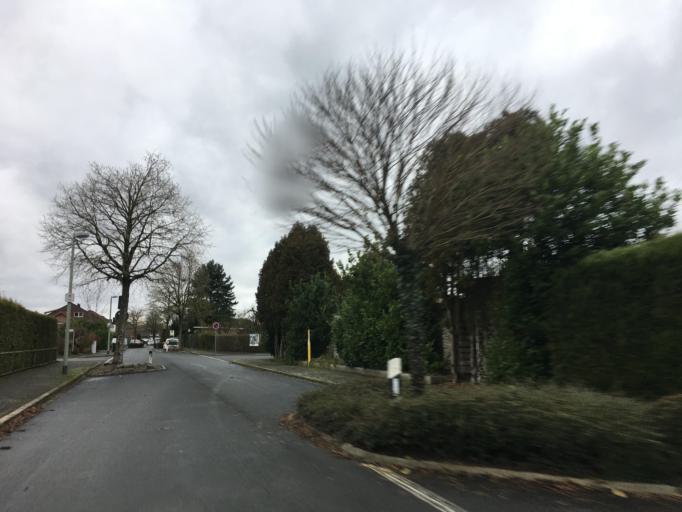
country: DE
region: North Rhine-Westphalia
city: Olfen
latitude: 51.7334
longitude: 7.2996
